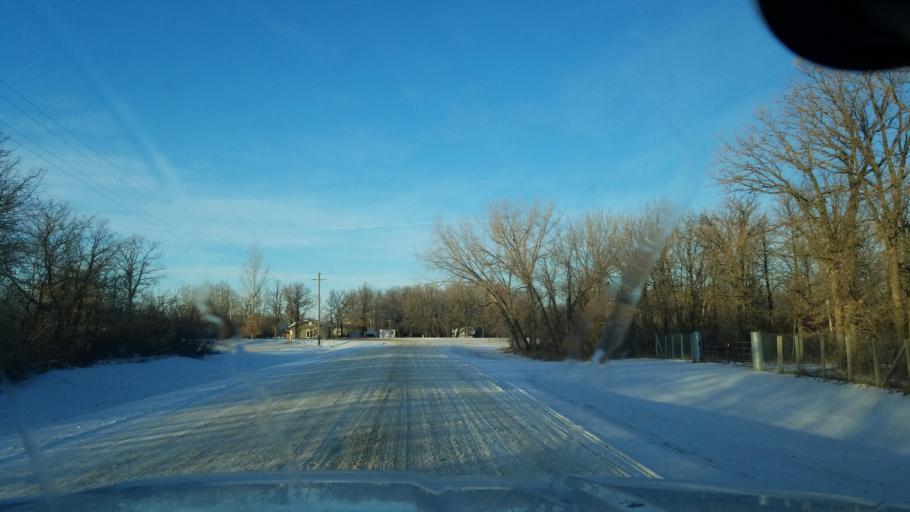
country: CA
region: Manitoba
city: Portage la Prairie
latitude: 49.9443
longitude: -98.3460
